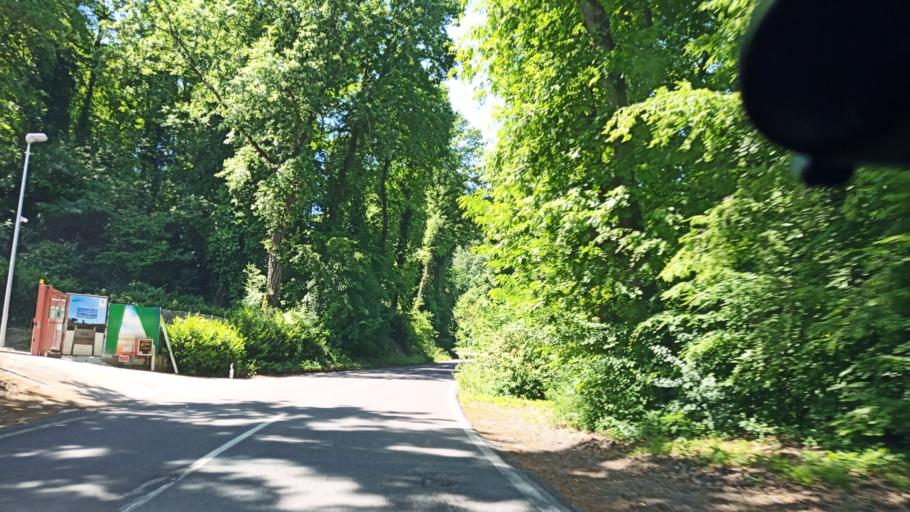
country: IT
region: Latium
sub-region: Provincia di Rieti
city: Stimigliano
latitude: 42.3075
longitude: 12.5661
